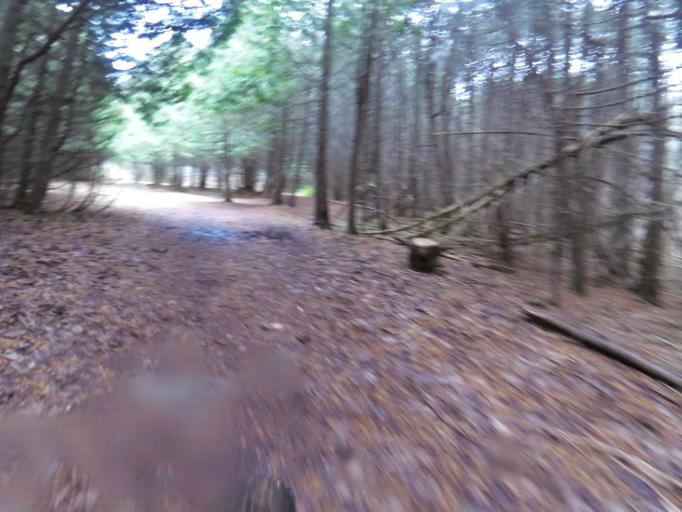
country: CA
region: Ontario
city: Bells Corners
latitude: 45.3036
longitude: -75.8110
